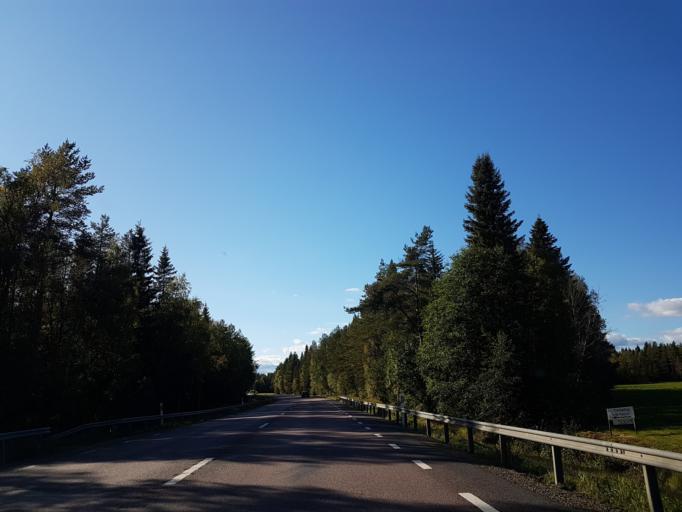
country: SE
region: Vaesterbotten
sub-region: Skelleftea Kommun
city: Burea
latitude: 64.3342
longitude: 21.2537
